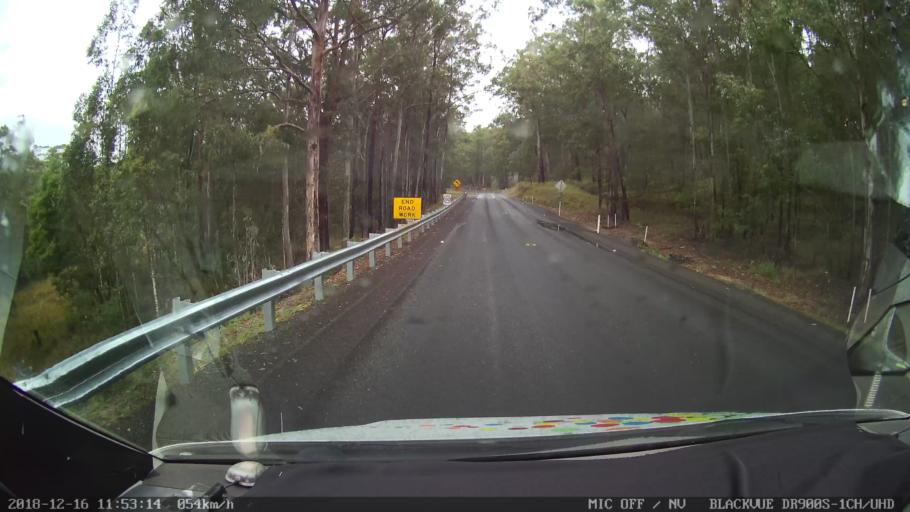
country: AU
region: New South Wales
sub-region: Tenterfield Municipality
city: Carrolls Creek
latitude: -28.9041
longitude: 152.2778
